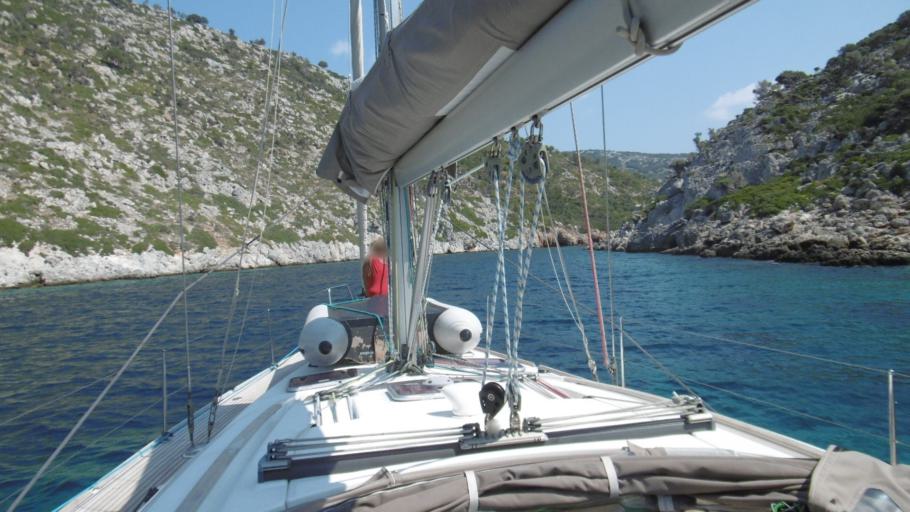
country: GR
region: Thessaly
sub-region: Nomos Magnisias
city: Patitirion
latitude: 39.3316
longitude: 24.0484
